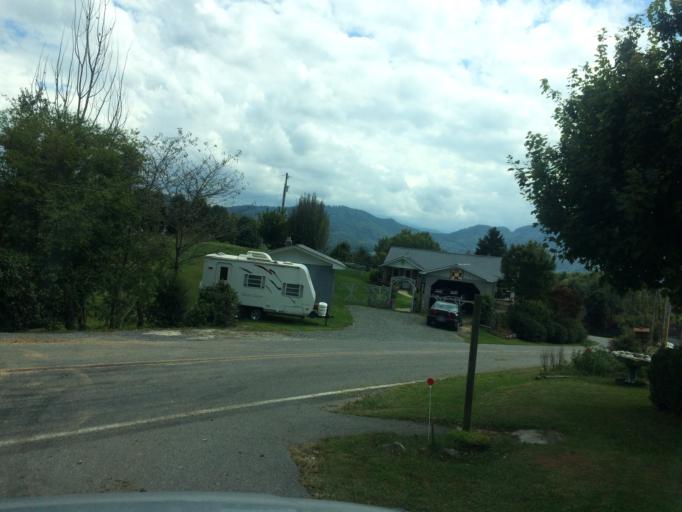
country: US
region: North Carolina
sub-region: Haywood County
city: Clyde
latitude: 35.5505
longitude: -82.9119
